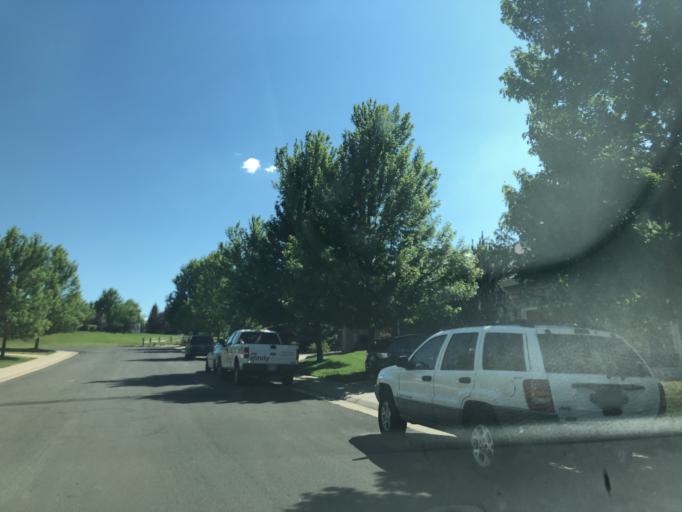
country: US
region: Colorado
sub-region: Arapahoe County
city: Dove Valley
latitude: 39.6090
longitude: -104.7876
